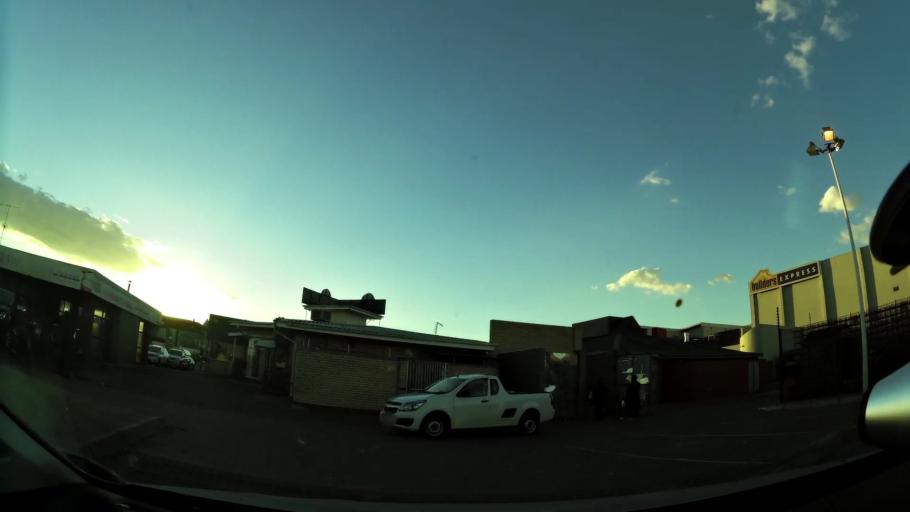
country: ZA
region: North-West
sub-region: Dr Kenneth Kaunda District Municipality
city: Potchefstroom
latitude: -26.7138
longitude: 27.1084
